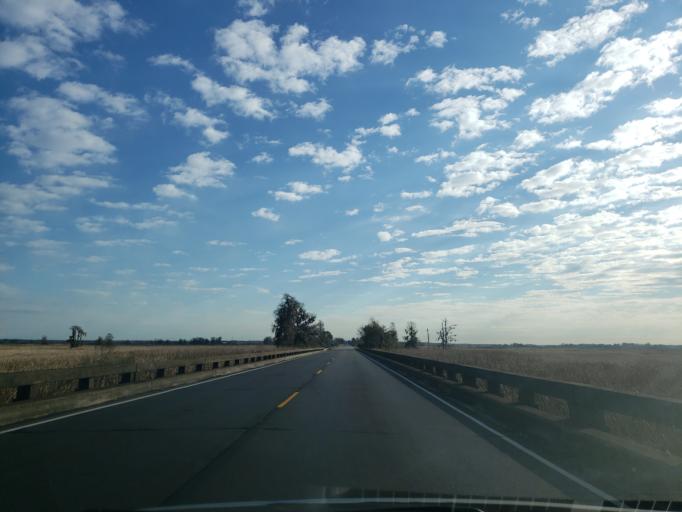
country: US
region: Georgia
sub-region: Chatham County
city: Port Wentworth
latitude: 32.1658
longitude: -81.1351
